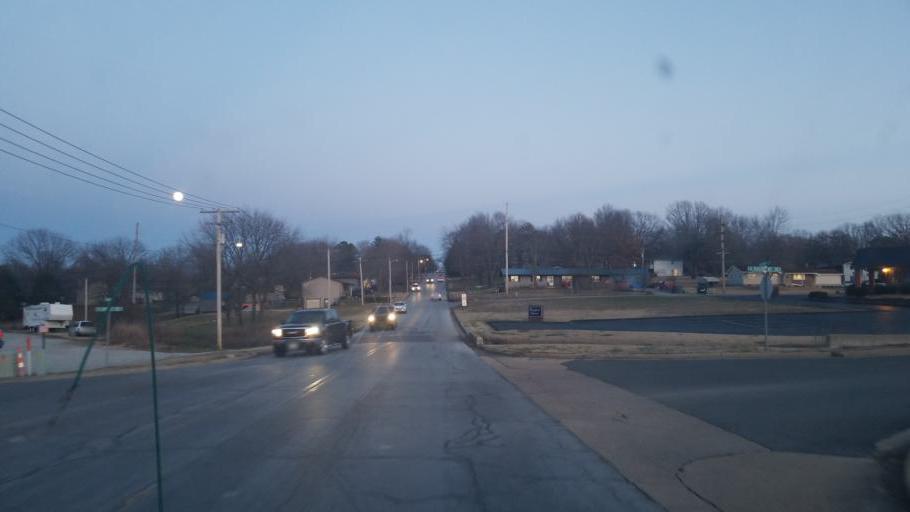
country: US
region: Missouri
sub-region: Howell County
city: West Plains
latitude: 36.7318
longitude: -91.8764
